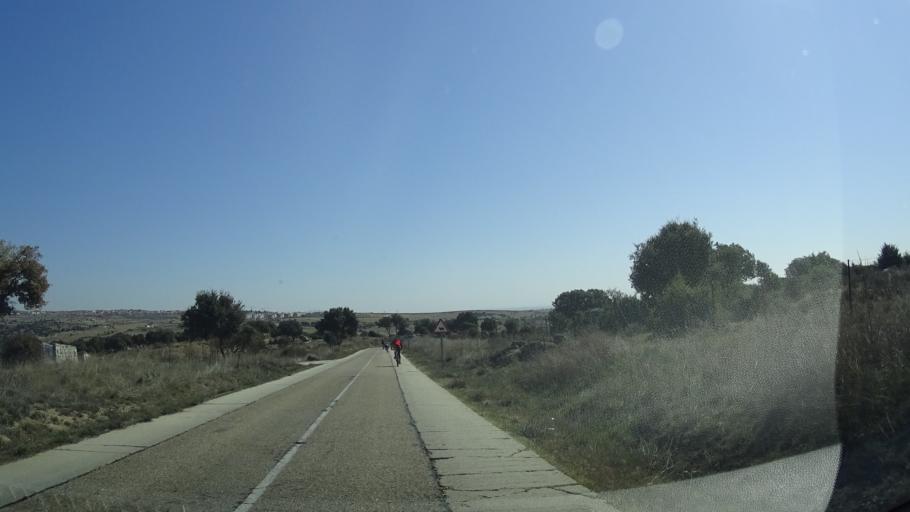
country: ES
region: Madrid
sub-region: Provincia de Madrid
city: Colmenar Viejo
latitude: 40.6442
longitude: -3.8159
